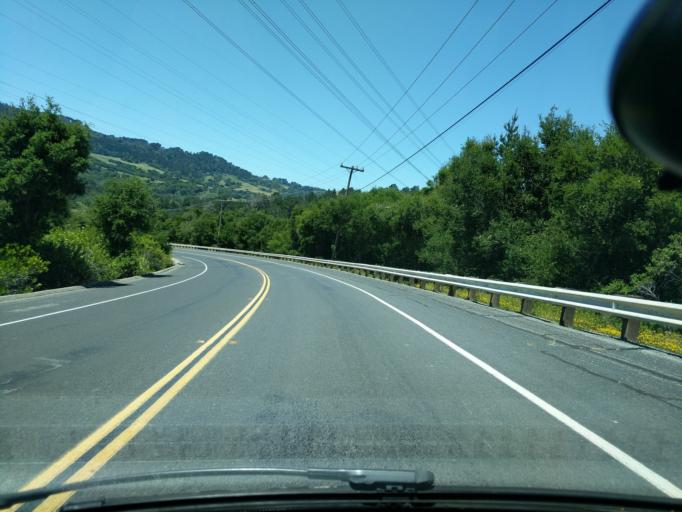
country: US
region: California
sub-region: Contra Costa County
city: Orinda
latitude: 37.9089
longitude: -122.2091
